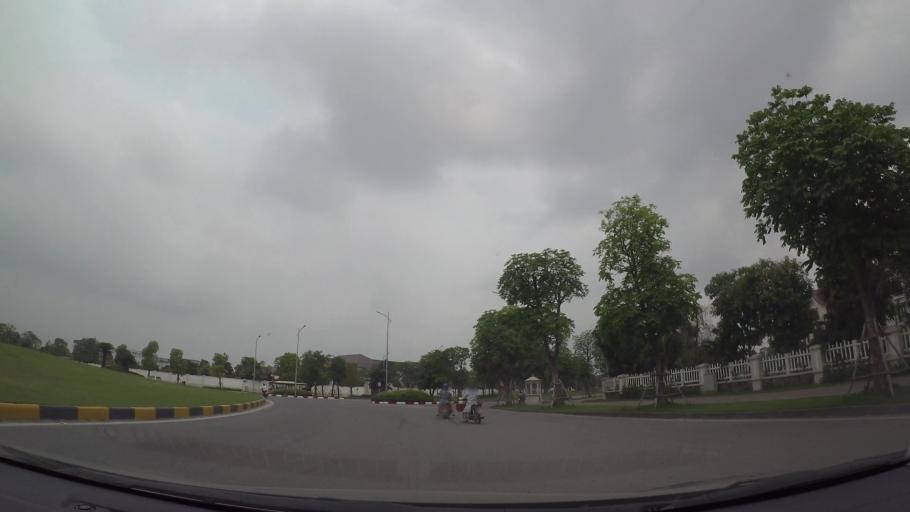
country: VN
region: Ha Noi
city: Trau Quy
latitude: 21.0466
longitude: 105.9108
